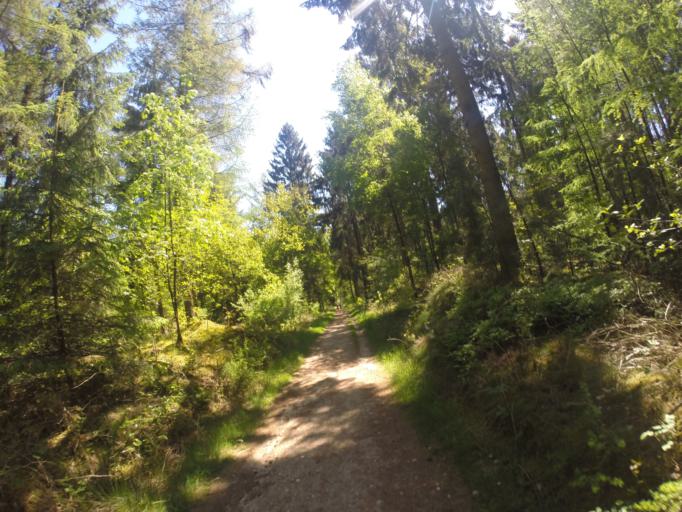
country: NL
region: Gelderland
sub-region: Gemeente Montferland
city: s-Heerenberg
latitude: 51.8902
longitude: 6.2060
